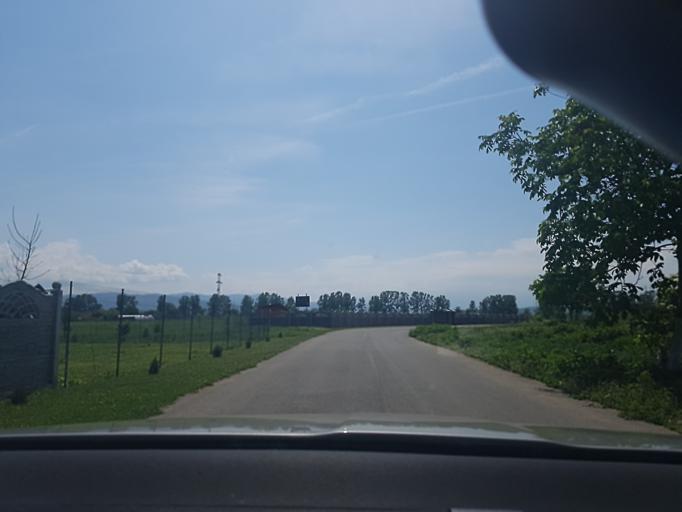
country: RO
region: Hunedoara
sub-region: Comuna Calan
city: Calan
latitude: 45.7407
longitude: 23.0042
